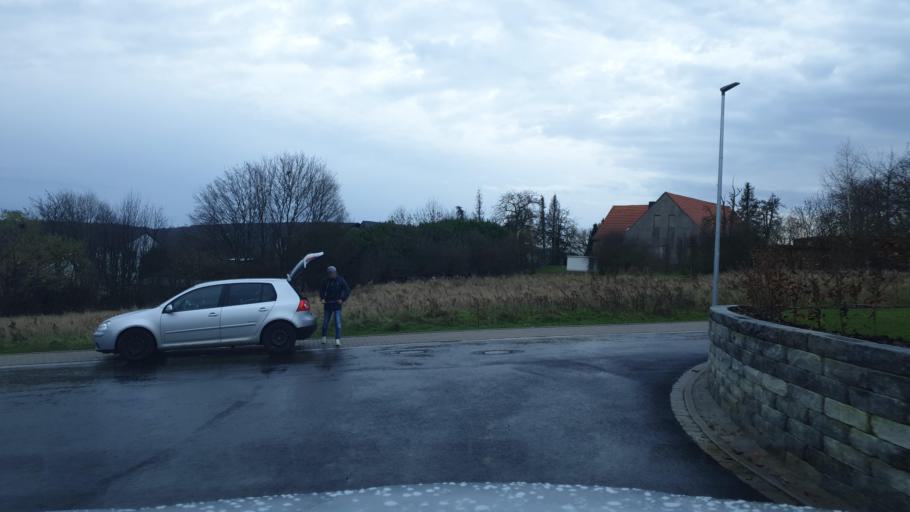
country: DE
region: North Rhine-Westphalia
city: Bad Oeynhausen
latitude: 52.1859
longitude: 8.8169
